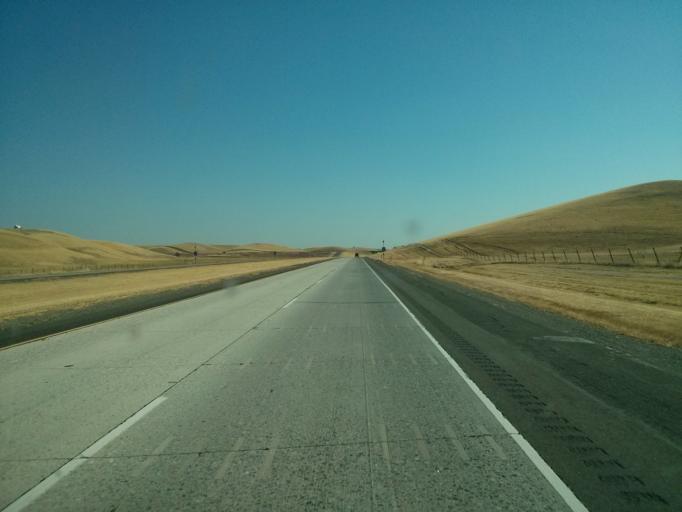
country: US
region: California
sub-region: Yolo County
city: Dunnigan
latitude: 38.7865
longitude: -121.9444
